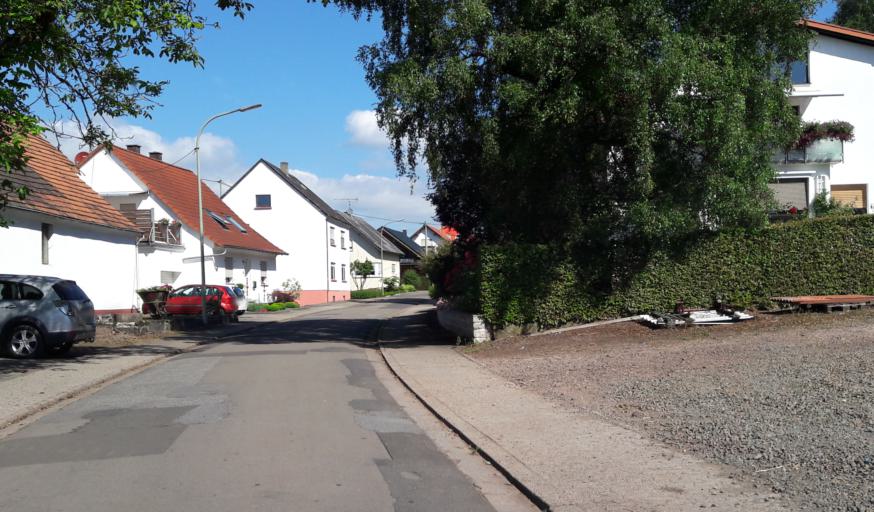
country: DE
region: Rheinland-Pfalz
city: Hahnweiler
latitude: 49.5548
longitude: 7.2021
